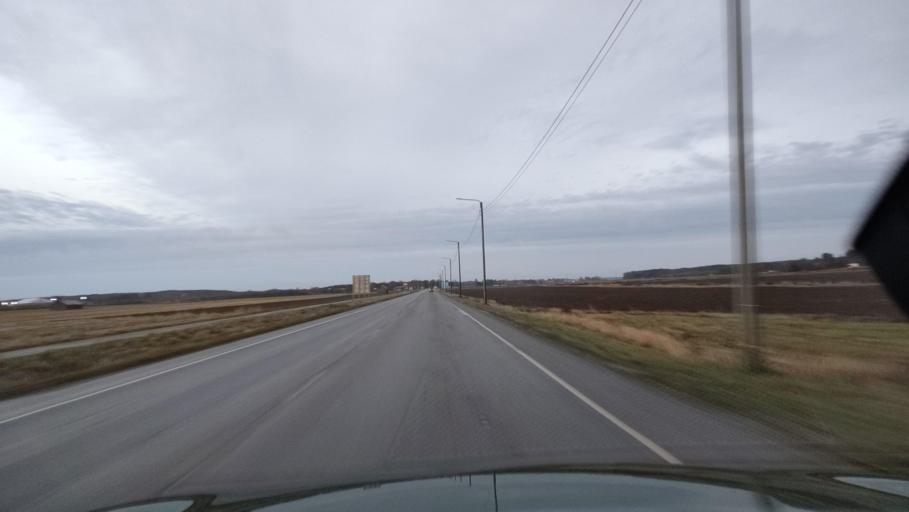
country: FI
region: Ostrobothnia
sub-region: Vaasa
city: Ristinummi
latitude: 63.0378
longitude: 21.7498
